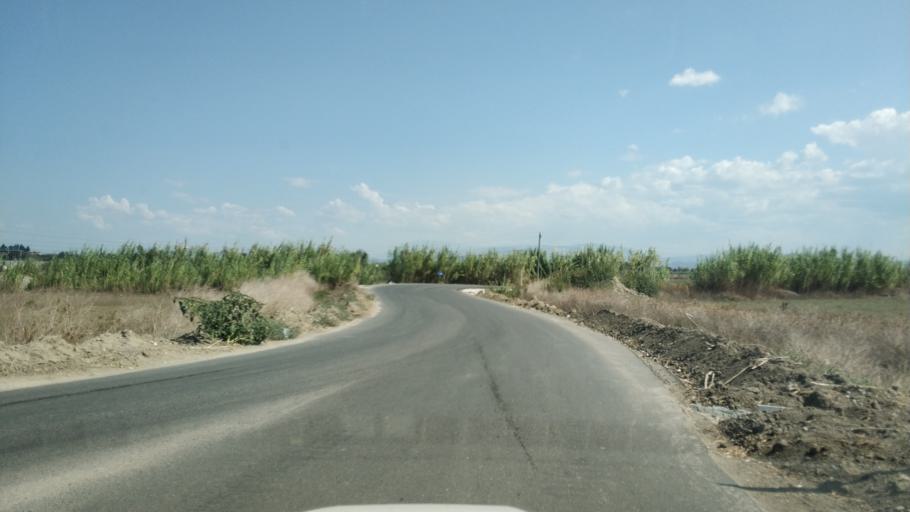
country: AL
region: Fier
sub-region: Rrethi i Fierit
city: Mbrostar-Ure
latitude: 40.7468
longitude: 19.5585
